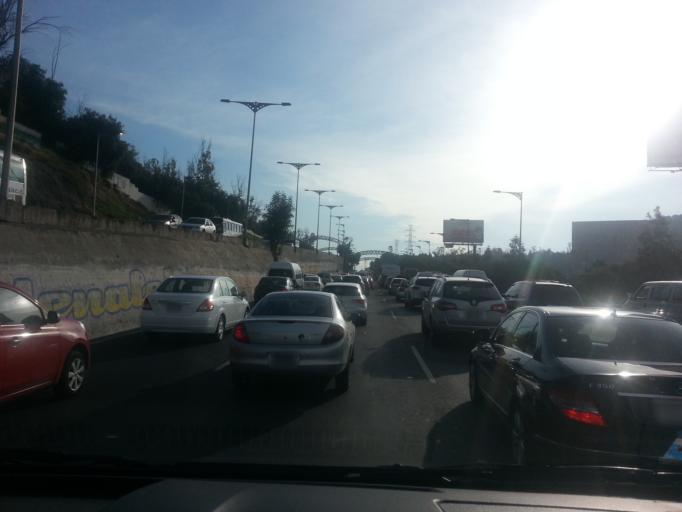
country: MX
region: Mexico City
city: Gustavo A. Madero
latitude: 19.5036
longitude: -99.1143
